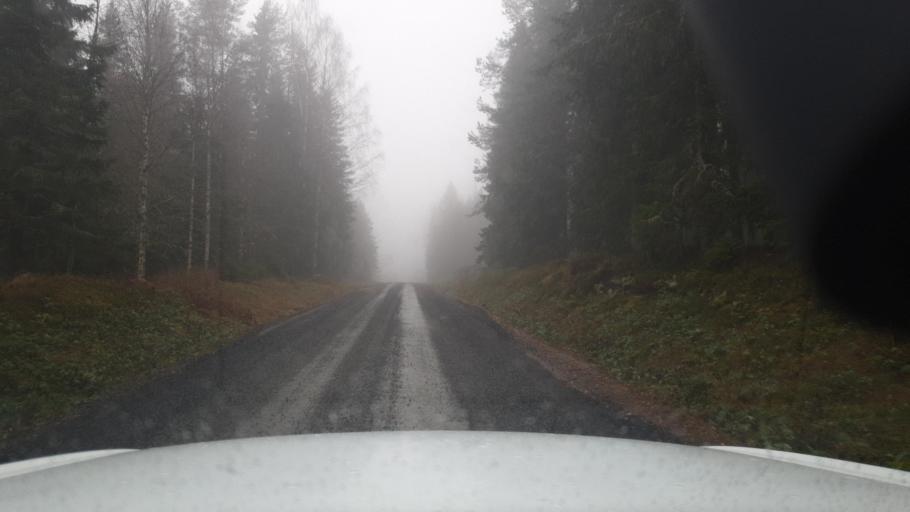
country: SE
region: Vaermland
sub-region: Torsby Kommun
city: Torsby
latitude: 60.1811
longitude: 12.6455
